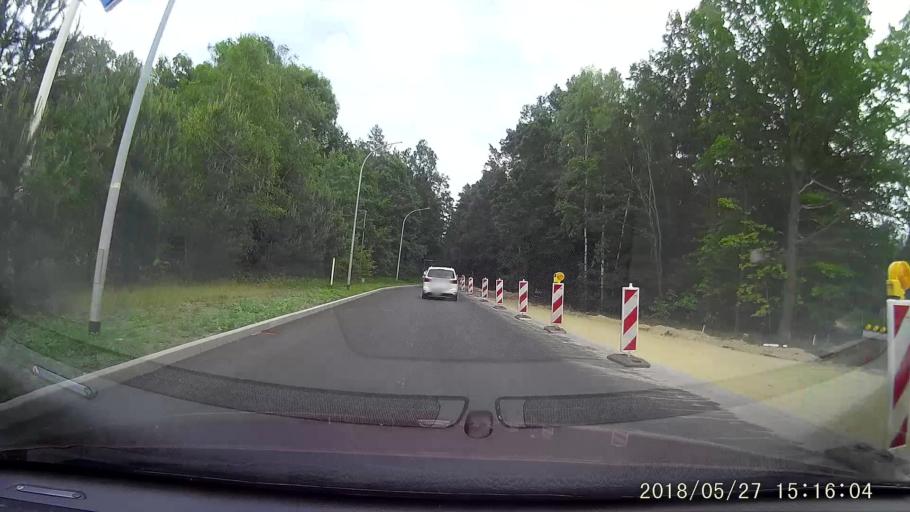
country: DE
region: Saxony
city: Niesky
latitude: 51.2790
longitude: 14.8192
